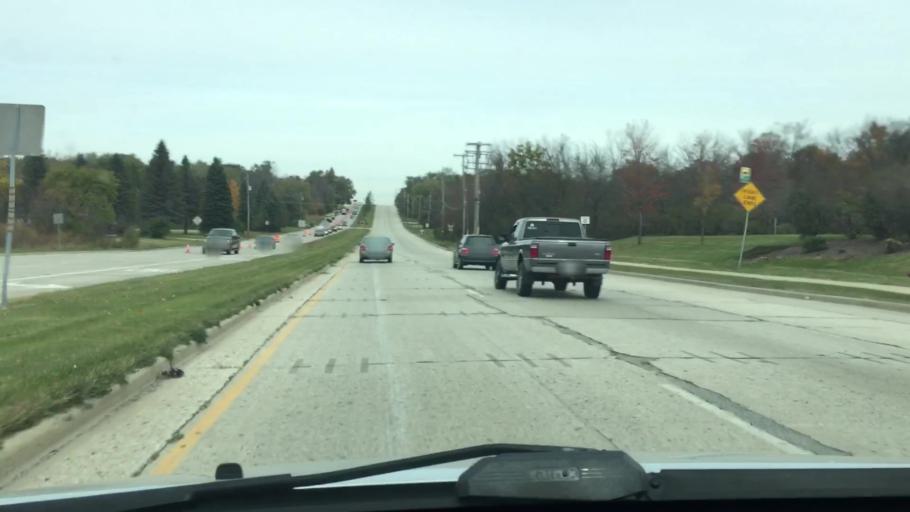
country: US
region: Wisconsin
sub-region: Waukesha County
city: New Berlin
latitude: 42.9584
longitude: -88.1089
